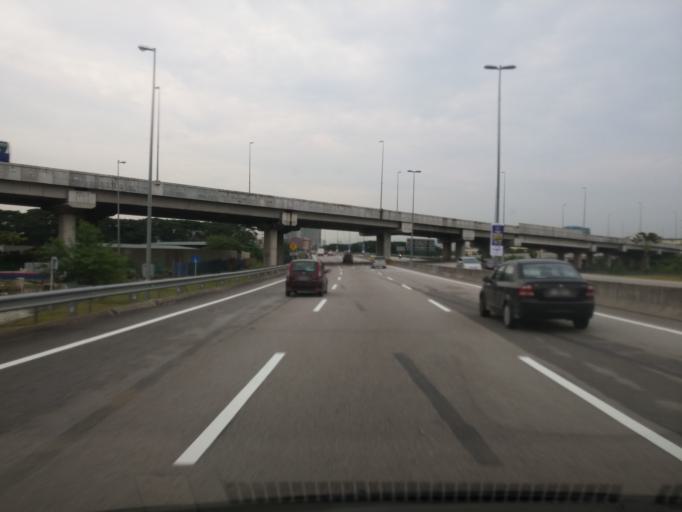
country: MY
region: Kuala Lumpur
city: Kuala Lumpur
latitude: 3.1134
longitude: 101.7144
